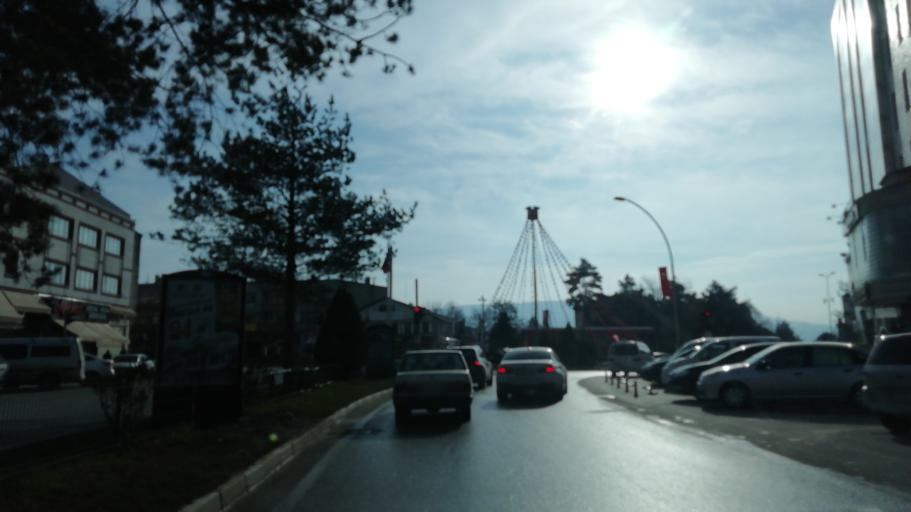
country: TR
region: Karabuk
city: Safranbolu
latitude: 41.2499
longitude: 32.6828
